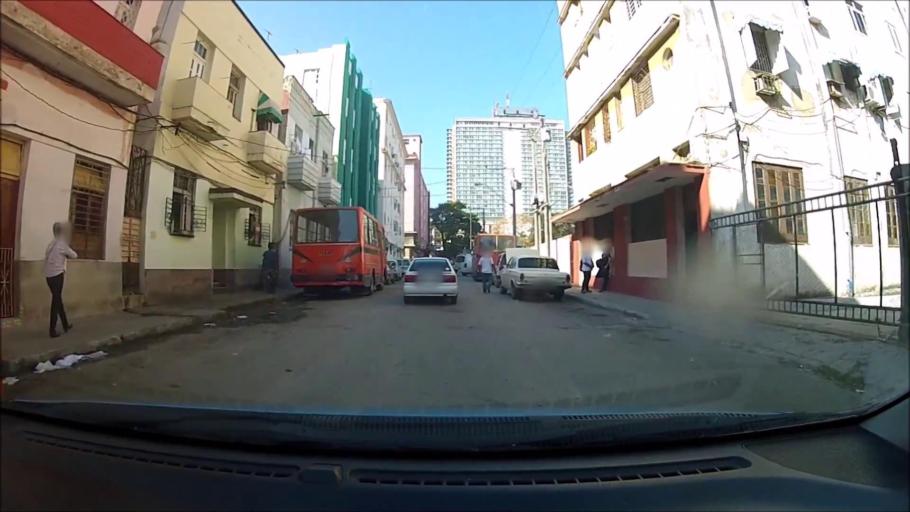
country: CU
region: La Habana
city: Havana
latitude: 23.1412
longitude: -82.3790
